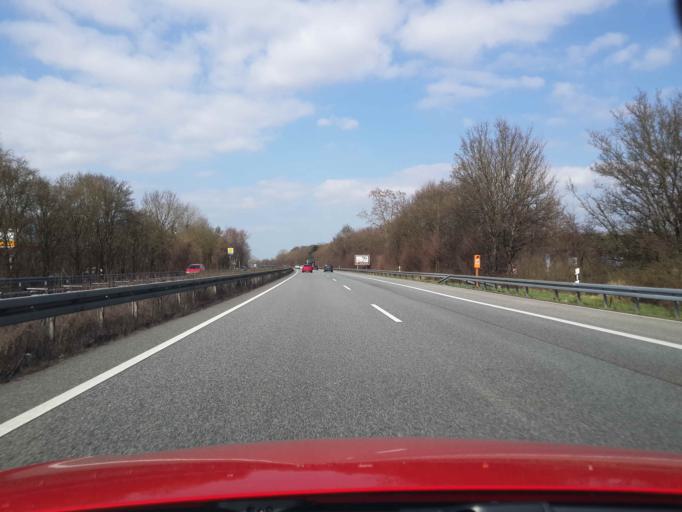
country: DE
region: Hesse
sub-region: Regierungsbezirk Darmstadt
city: Buttelborn
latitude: 49.8928
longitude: 8.5452
